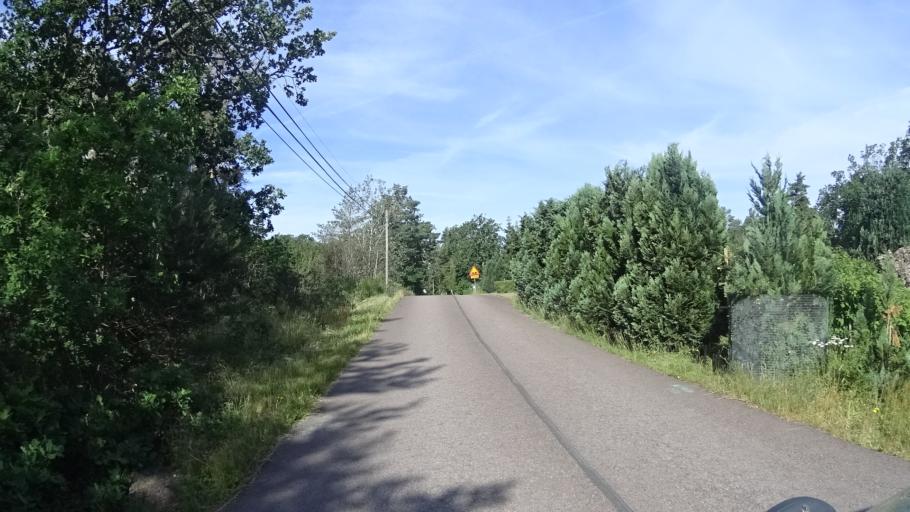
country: SE
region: Kalmar
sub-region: Oskarshamns Kommun
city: Oskarshamn
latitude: 57.2319
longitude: 16.4871
